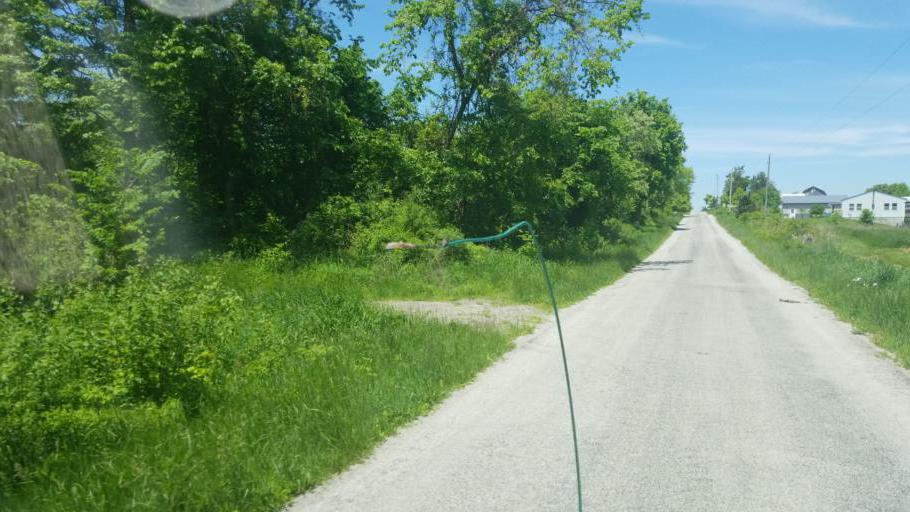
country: US
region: Ohio
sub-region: Huron County
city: Greenwich
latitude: 40.9981
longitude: -82.4331
